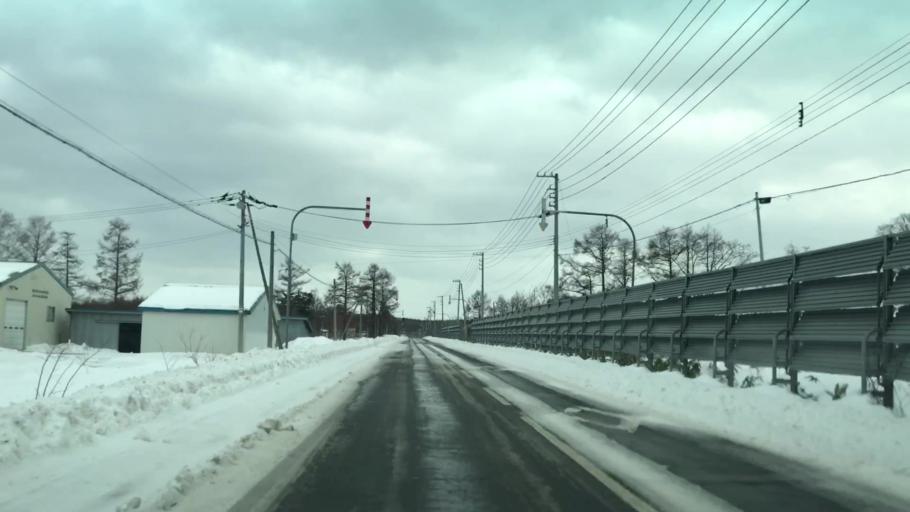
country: JP
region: Hokkaido
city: Yoichi
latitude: 43.3103
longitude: 140.5495
